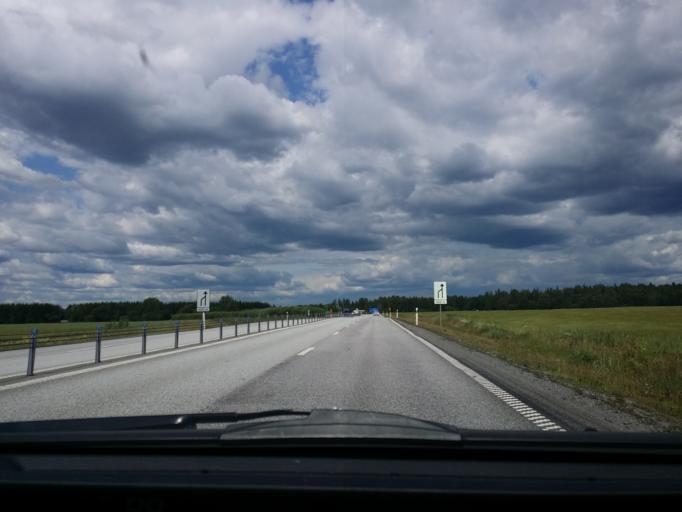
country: SE
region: OErebro
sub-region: Orebro Kommun
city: Hovsta
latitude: 59.4174
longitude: 15.1786
